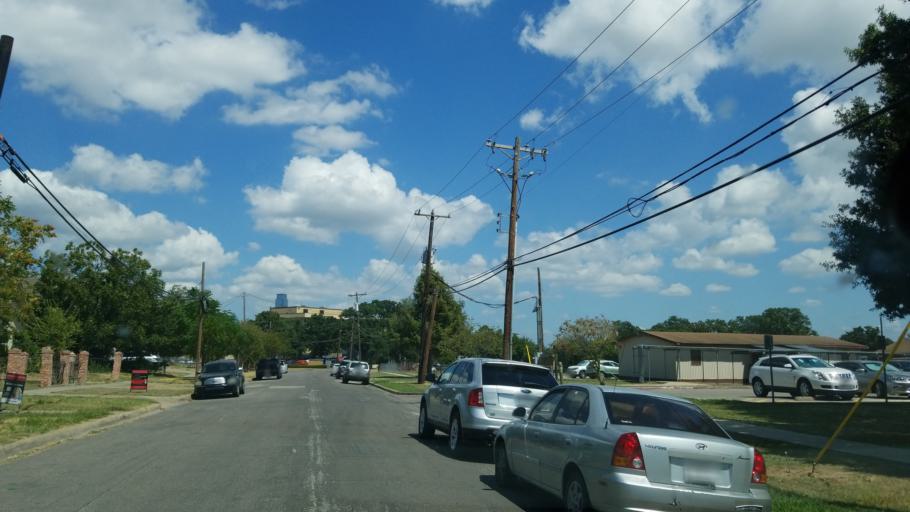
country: US
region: Texas
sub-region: Dallas County
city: Dallas
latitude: 32.7571
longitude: -96.8256
